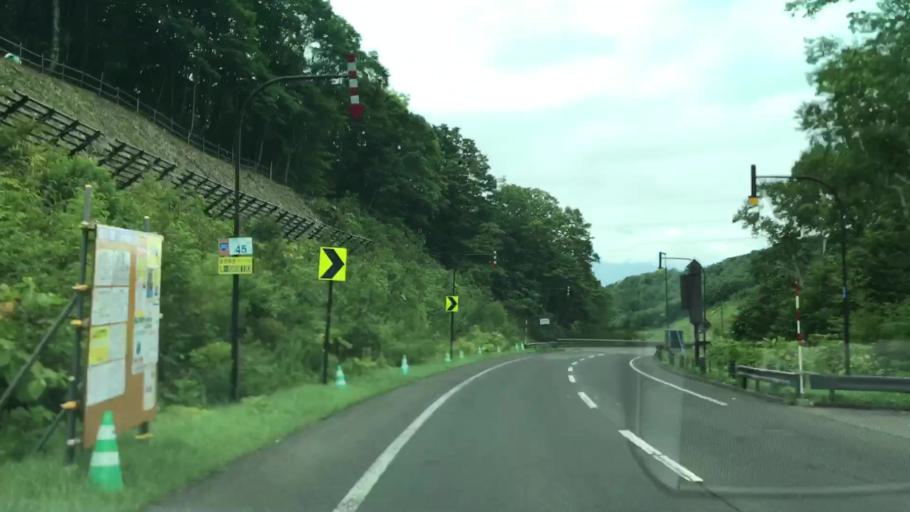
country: JP
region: Hokkaido
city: Otaru
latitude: 42.9613
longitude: 140.8781
